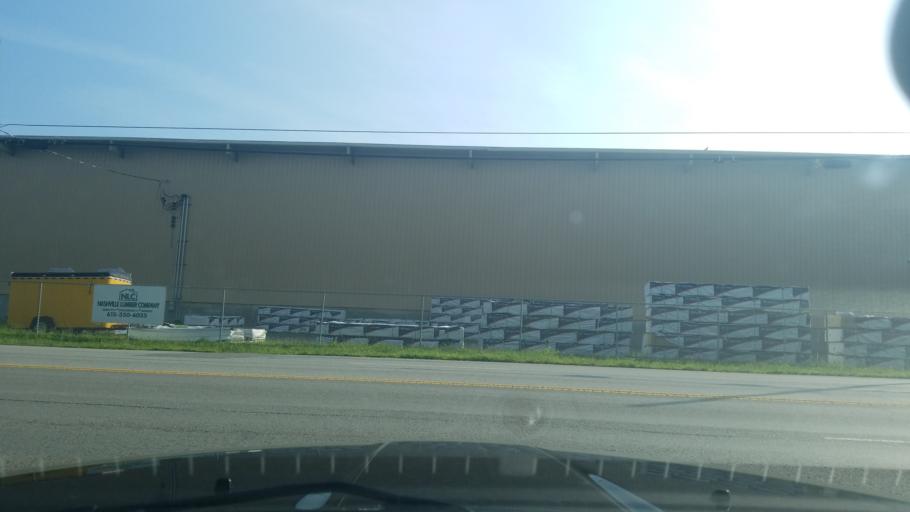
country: US
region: Tennessee
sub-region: Davidson County
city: Nashville
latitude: 36.1638
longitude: -86.8519
